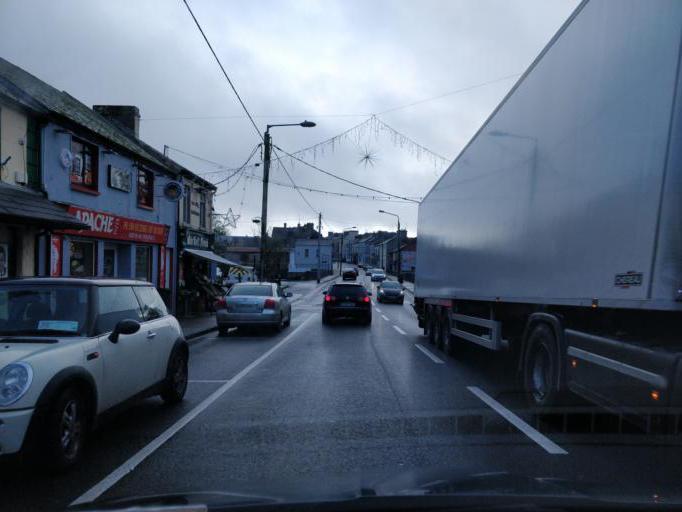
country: IE
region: Connaught
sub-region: Roscommon
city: Castlerea
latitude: 53.7685
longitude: -8.4918
